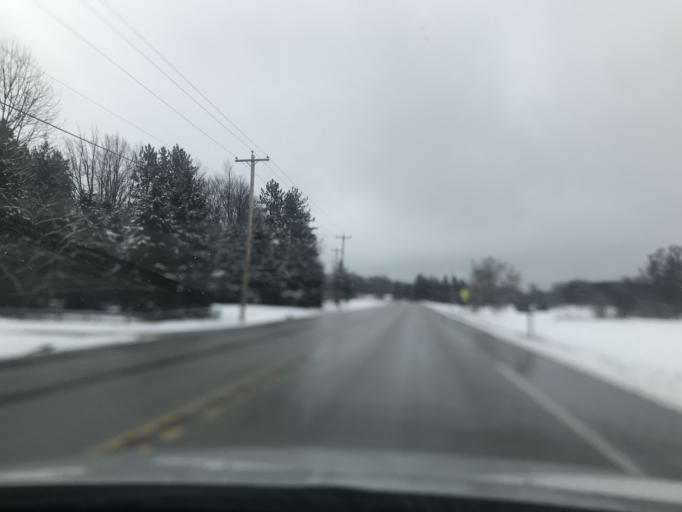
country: US
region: Wisconsin
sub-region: Marinette County
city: Peshtigo
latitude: 45.1764
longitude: -87.7388
